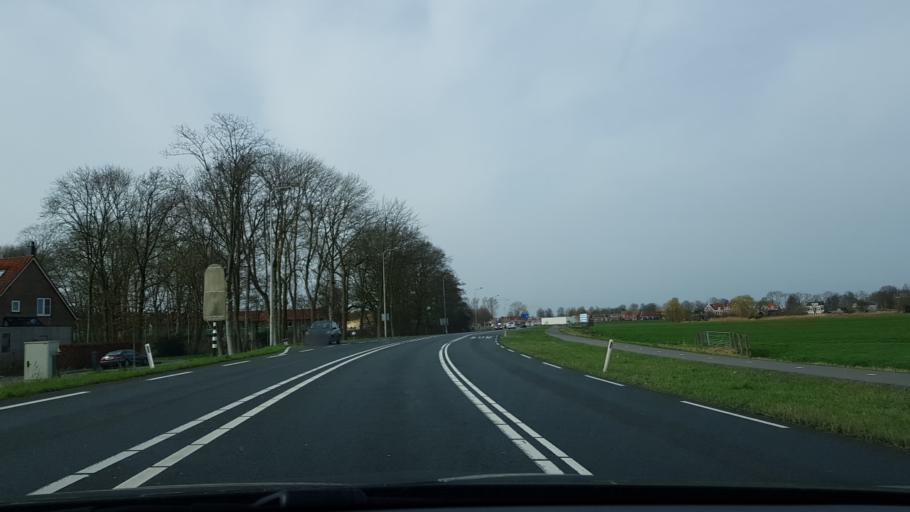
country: NL
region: North Holland
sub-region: Gemeente Ouder-Amstel
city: Ouderkerk aan de Amstel
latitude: 52.2989
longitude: 4.9084
